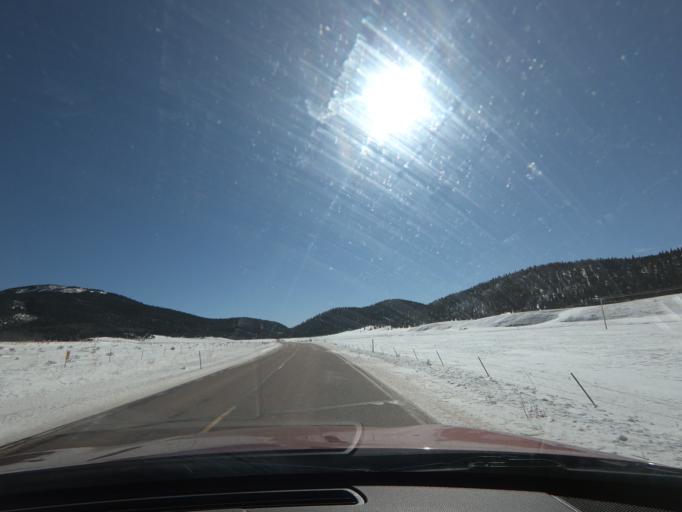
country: US
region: Colorado
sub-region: Teller County
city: Cripple Creek
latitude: 38.7641
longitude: -105.1157
